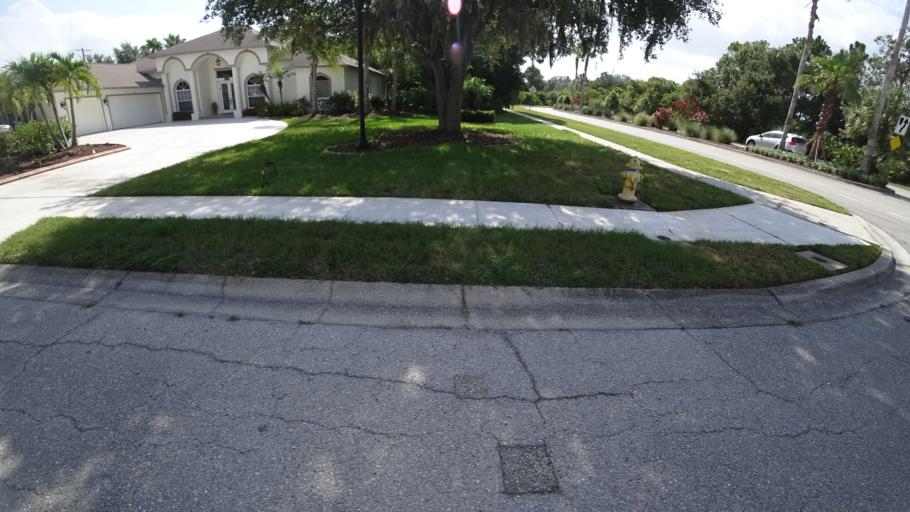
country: US
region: Florida
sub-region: Sarasota County
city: The Meadows
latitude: 27.4032
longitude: -82.4332
